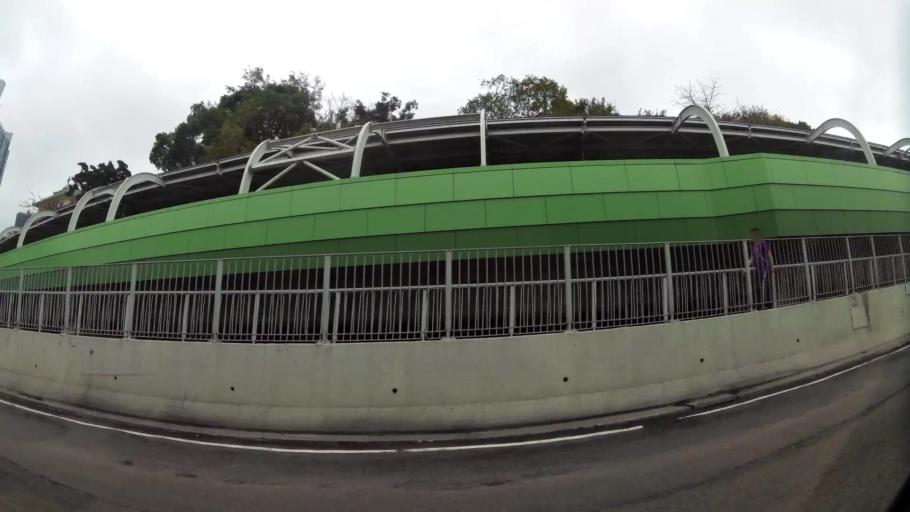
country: HK
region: Central and Western
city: Central
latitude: 22.2466
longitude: 114.1609
